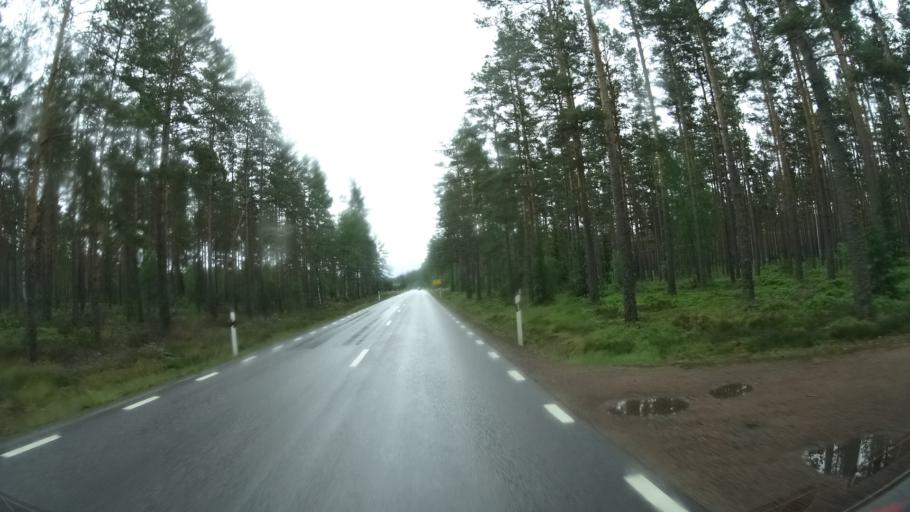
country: SE
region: Kalmar
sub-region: Hultsfreds Kommun
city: Hultsfred
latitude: 57.5149
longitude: 15.8190
